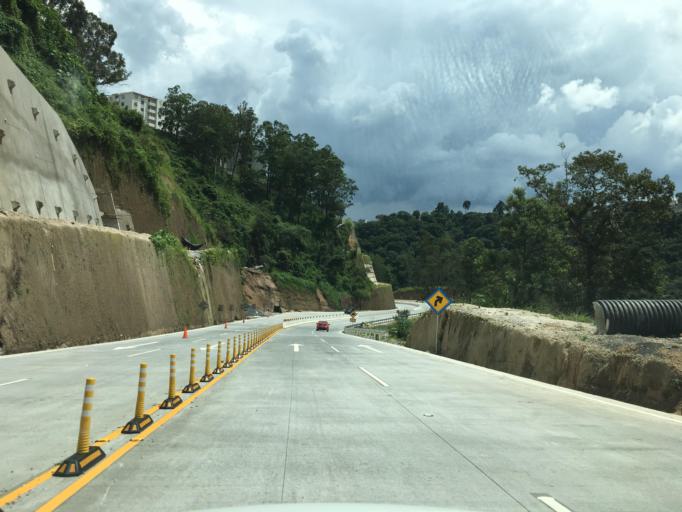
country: GT
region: Guatemala
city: Santa Catarina Pinula
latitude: 14.5663
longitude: -90.5398
